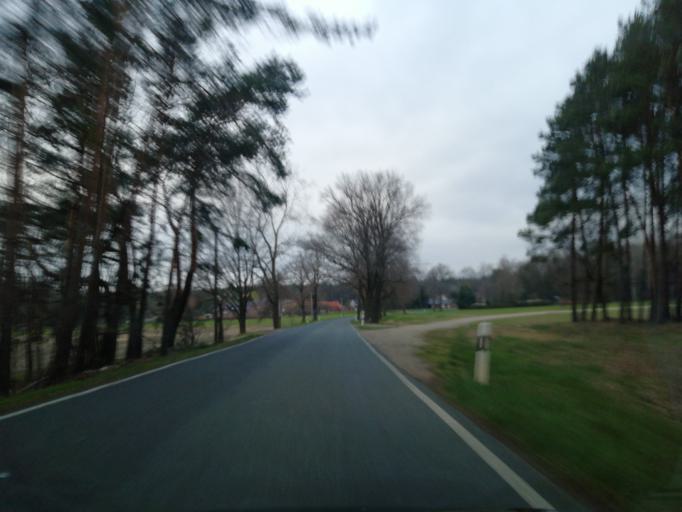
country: DE
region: Brandenburg
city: Vetschau
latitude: 51.7652
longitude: 14.0846
